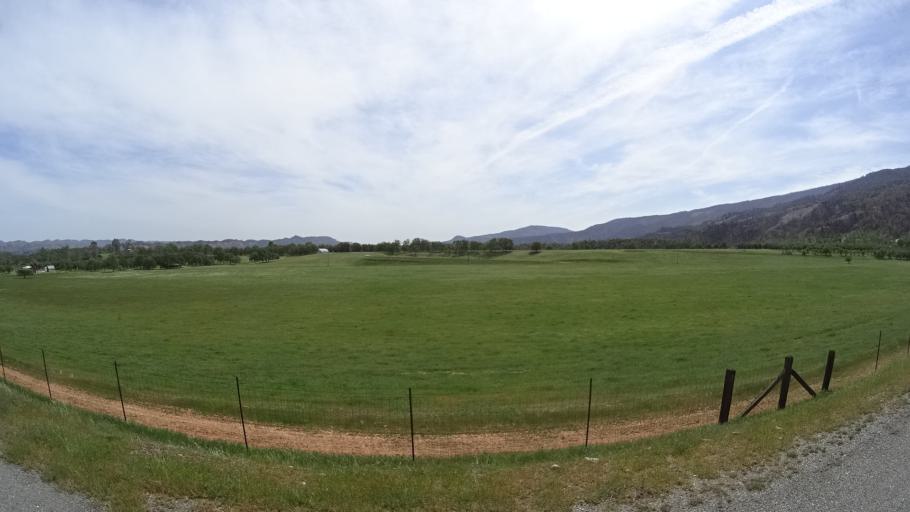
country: US
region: California
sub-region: Glenn County
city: Willows
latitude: 39.5763
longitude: -122.6100
